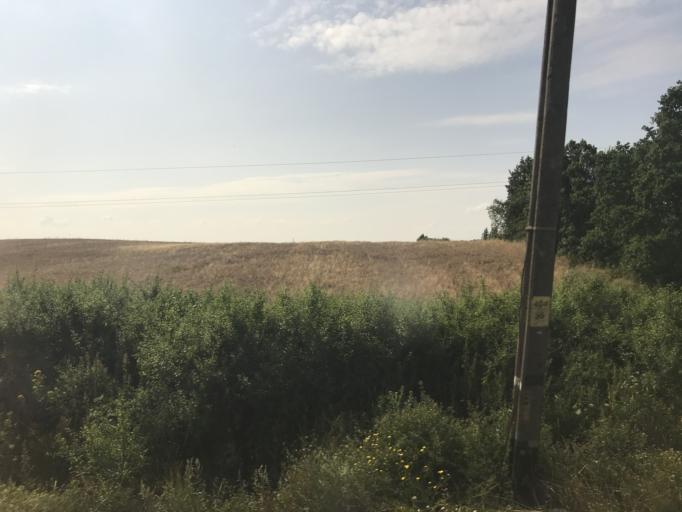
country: PL
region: Kujawsko-Pomorskie
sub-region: Powiat swiecki
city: Bukowiec
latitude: 53.3758
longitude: 18.2849
